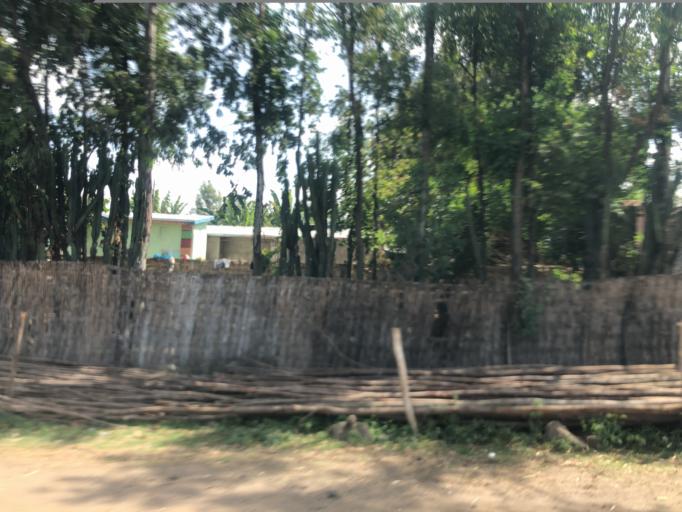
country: ET
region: Oromiya
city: Shashemene
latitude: 7.2280
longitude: 38.6308
